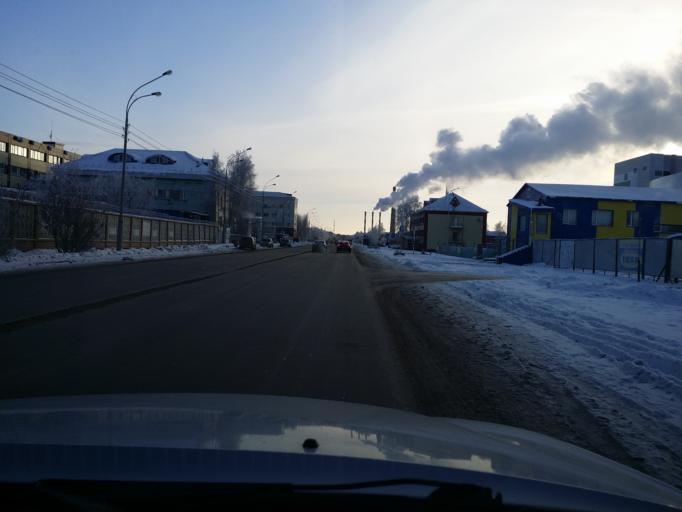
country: RU
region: Khanty-Mansiyskiy Avtonomnyy Okrug
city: Nizhnevartovsk
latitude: 60.9424
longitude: 76.5483
